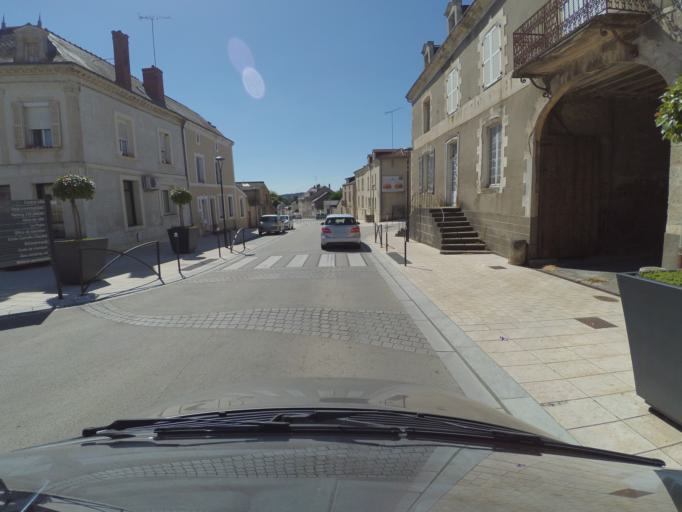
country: FR
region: Pays de la Loire
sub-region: Departement de Maine-et-Loire
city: Vihiers
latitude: 47.1468
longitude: -0.5343
